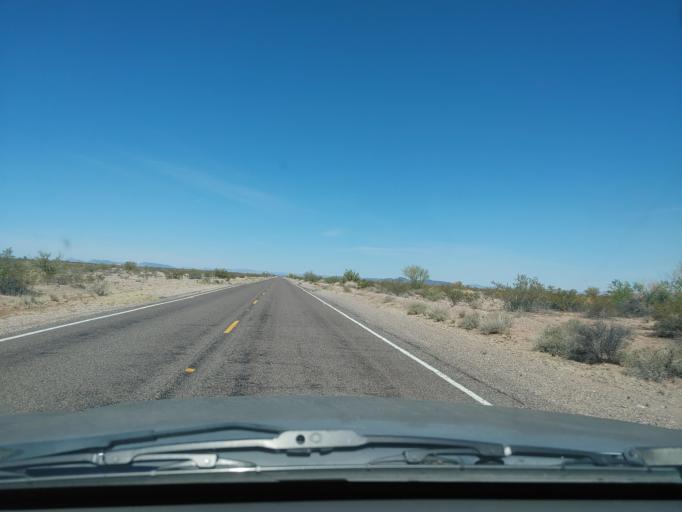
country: US
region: Arizona
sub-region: Maricopa County
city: Gila Bend
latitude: 32.8875
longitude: -113.2365
